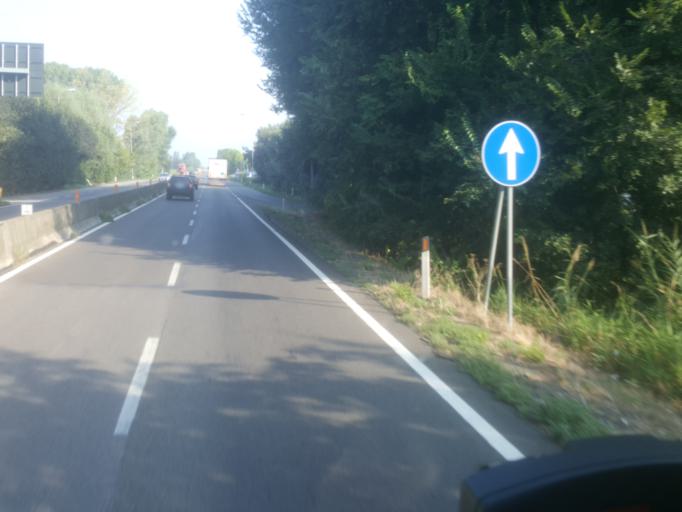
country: IT
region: Emilia-Romagna
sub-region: Provincia di Ravenna
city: Ravenna
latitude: 44.4002
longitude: 12.1802
